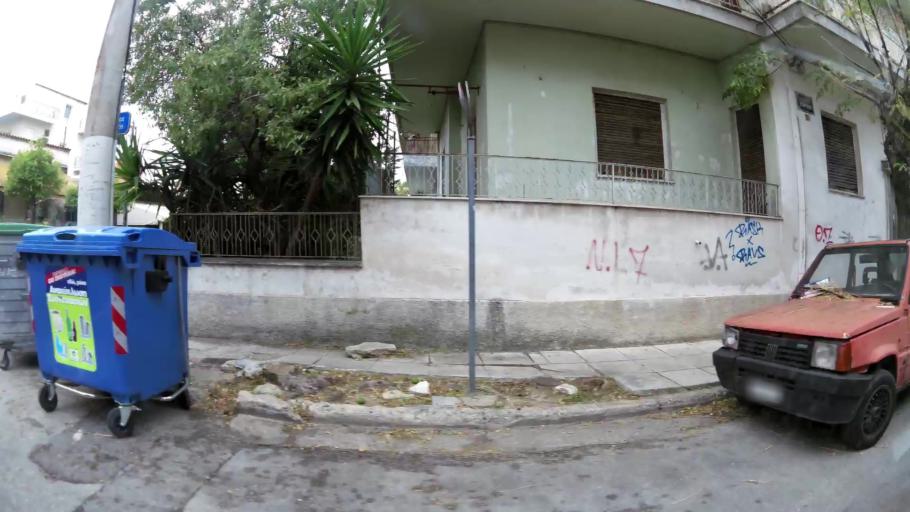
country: GR
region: Attica
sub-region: Nomarchia Athinas
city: Ilion
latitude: 38.0301
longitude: 23.7087
